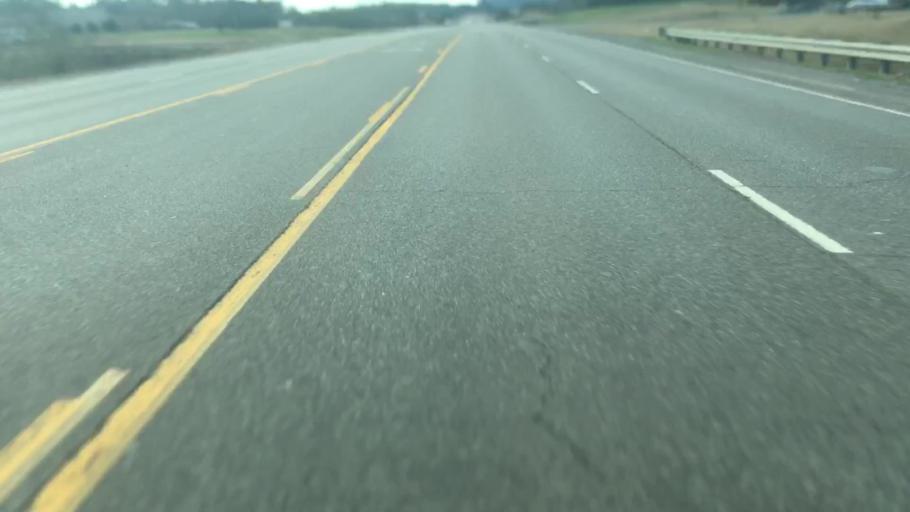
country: US
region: Alabama
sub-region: Walker County
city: Jasper
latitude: 33.8129
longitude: -87.2334
